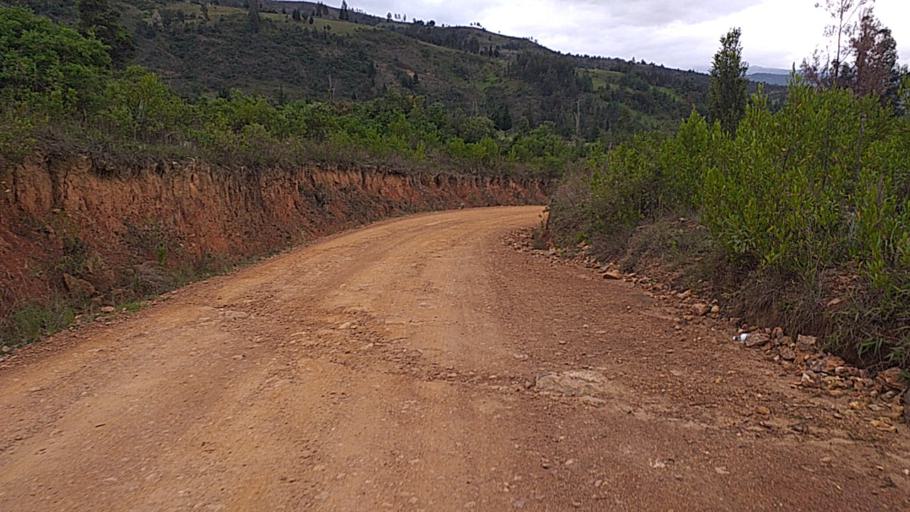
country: CO
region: Boyaca
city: Floresta
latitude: 5.8806
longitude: -72.9108
